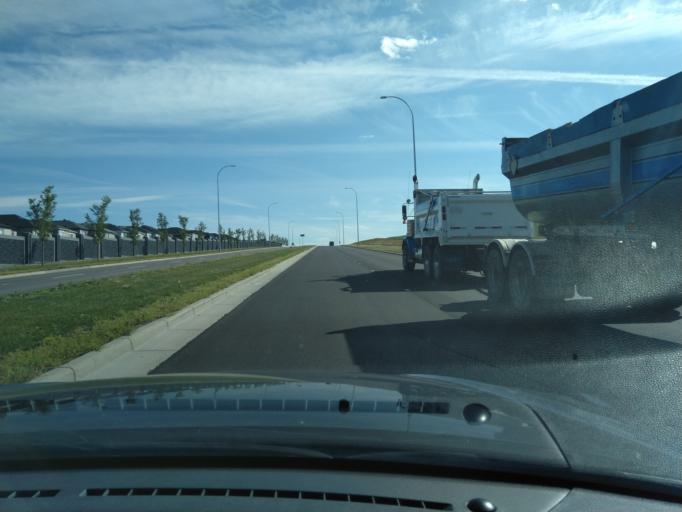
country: CA
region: Alberta
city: Calgary
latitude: 51.1788
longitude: -114.1761
